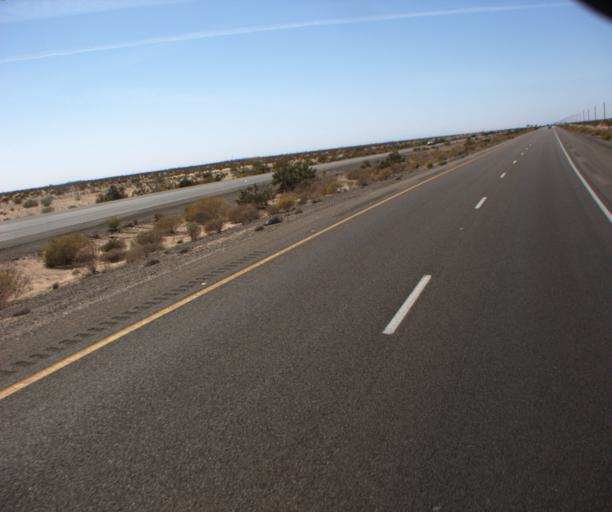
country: US
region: Arizona
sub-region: Yuma County
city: Somerton
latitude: 32.4948
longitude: -114.6628
